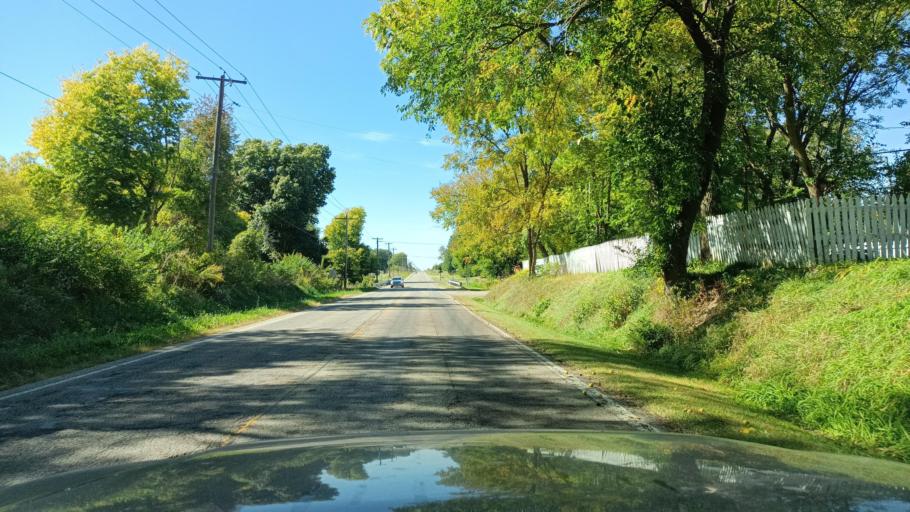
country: US
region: Illinois
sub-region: Champaign County
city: Mahomet
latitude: 40.1952
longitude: -88.4249
